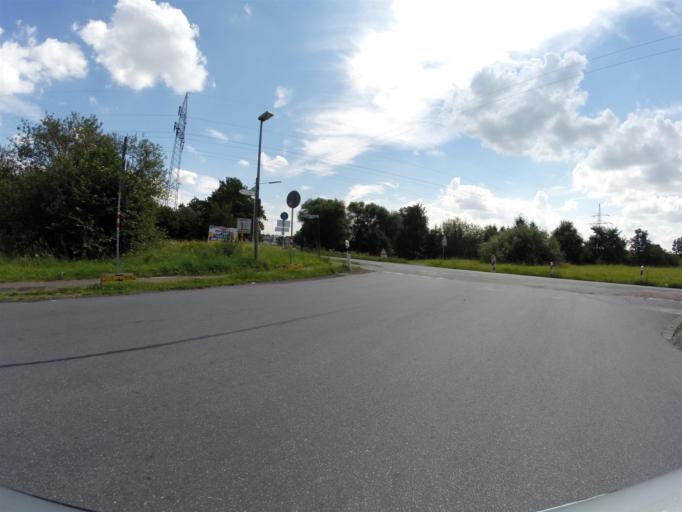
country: DE
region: North Rhine-Westphalia
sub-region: Regierungsbezirk Detmold
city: Herford
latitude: 52.1318
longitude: 8.6584
